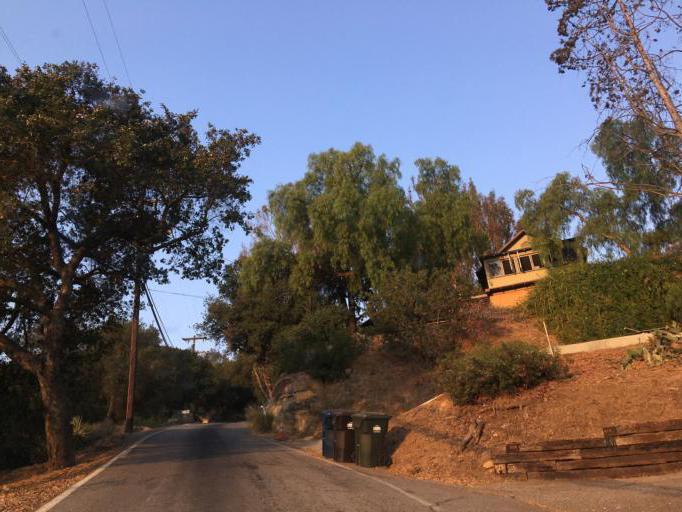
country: US
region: California
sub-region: Los Angeles County
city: Topanga
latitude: 34.0767
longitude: -118.6017
